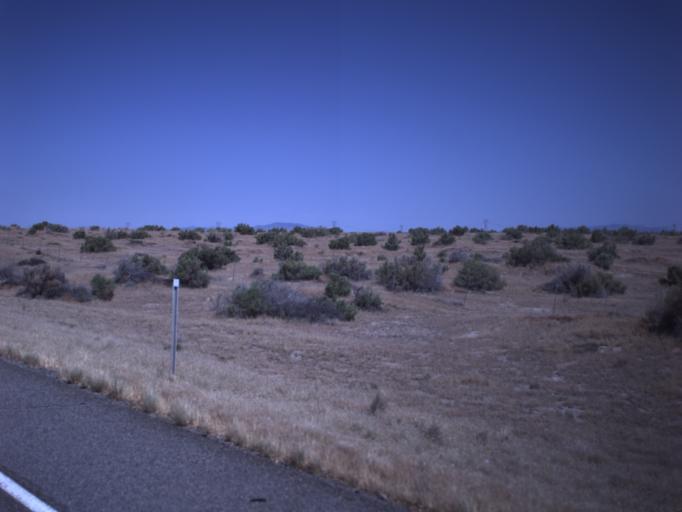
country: US
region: Utah
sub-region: Millard County
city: Delta
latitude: 39.4752
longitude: -112.4843
